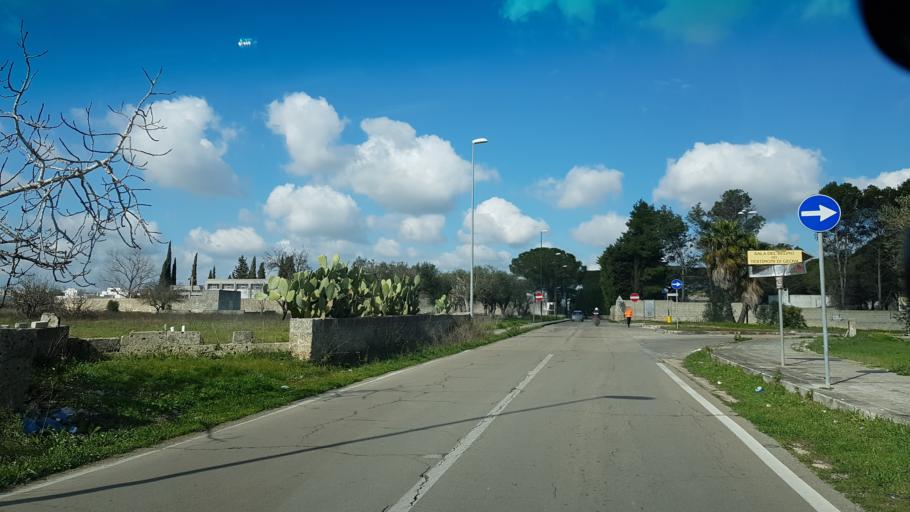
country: IT
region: Apulia
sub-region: Provincia di Lecce
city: Campi Salentina
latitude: 40.3938
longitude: 18.0291
